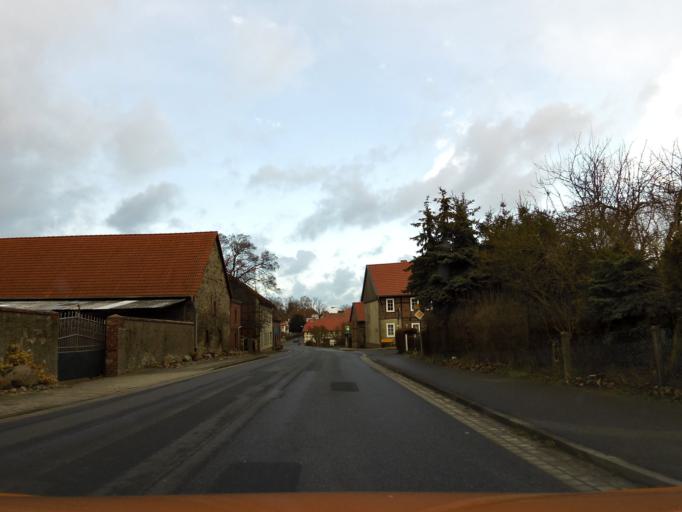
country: DE
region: Lower Saxony
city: Gross Twulpstedt
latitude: 52.3706
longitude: 10.9206
